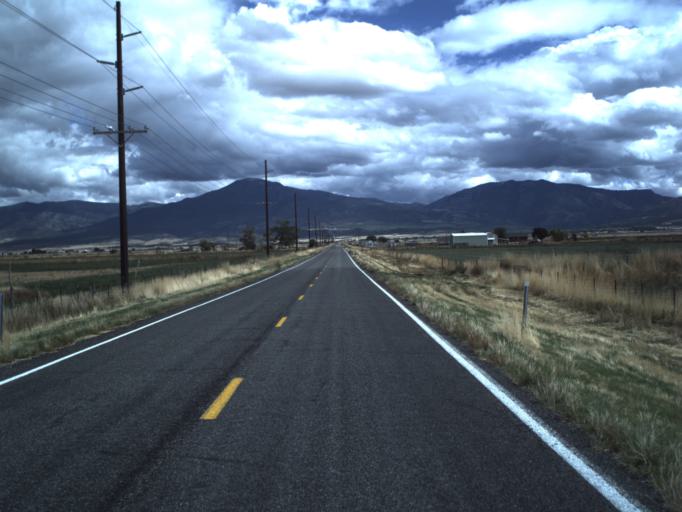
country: US
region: Utah
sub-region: Millard County
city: Fillmore
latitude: 38.9792
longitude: -112.4057
